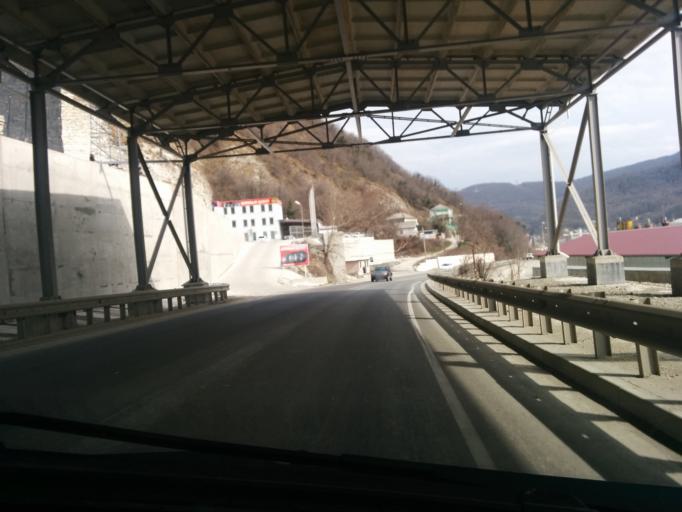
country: RU
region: Krasnodarskiy
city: Tuapse
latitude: 44.1169
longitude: 39.1077
